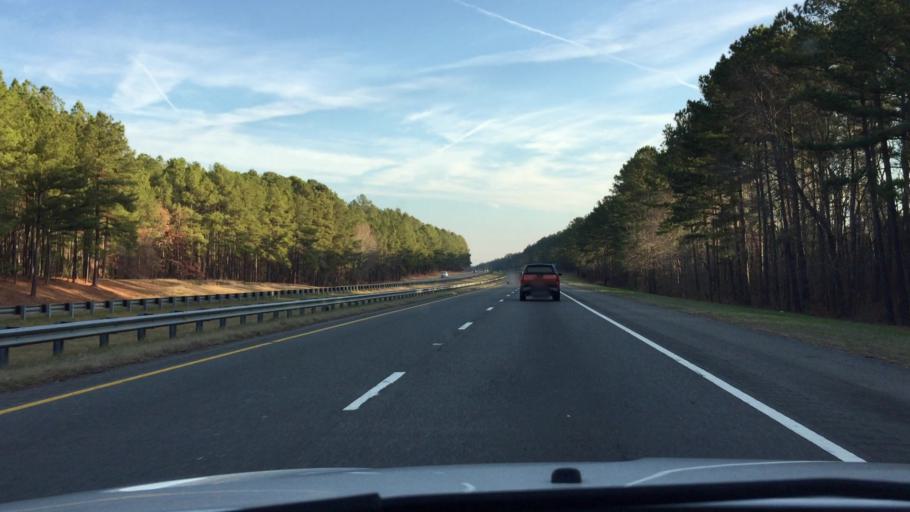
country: US
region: North Carolina
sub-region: Chatham County
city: Farmville
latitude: 35.5429
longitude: -79.1693
